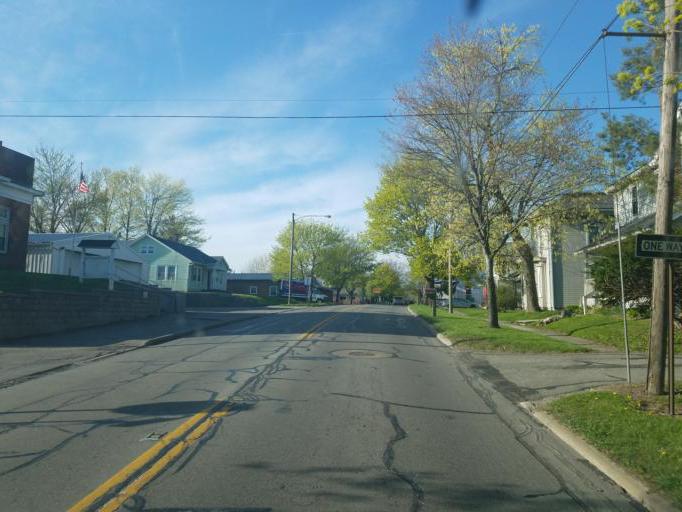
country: US
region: Ohio
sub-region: Ashland County
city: Ashland
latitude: 40.9642
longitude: -82.3648
